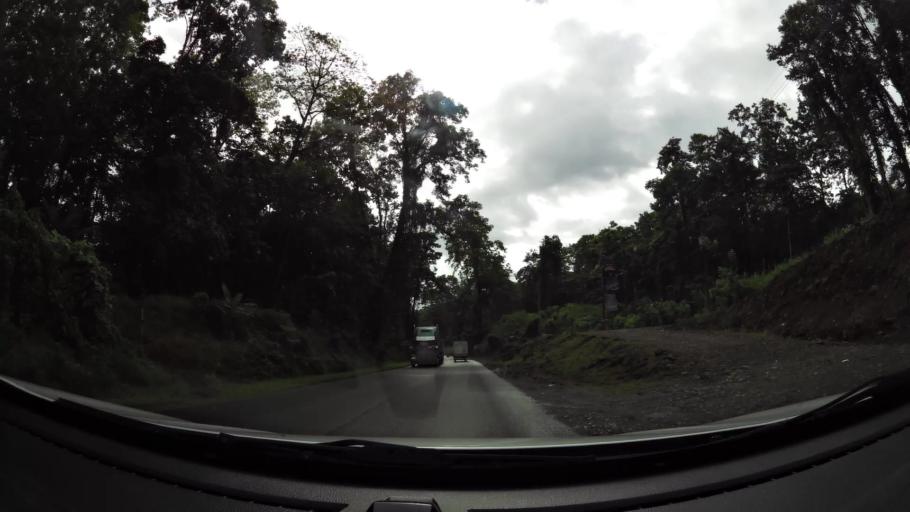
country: CR
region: Limon
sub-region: Canton de Siquirres
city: Siquirres
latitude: 10.1043
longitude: -83.5290
